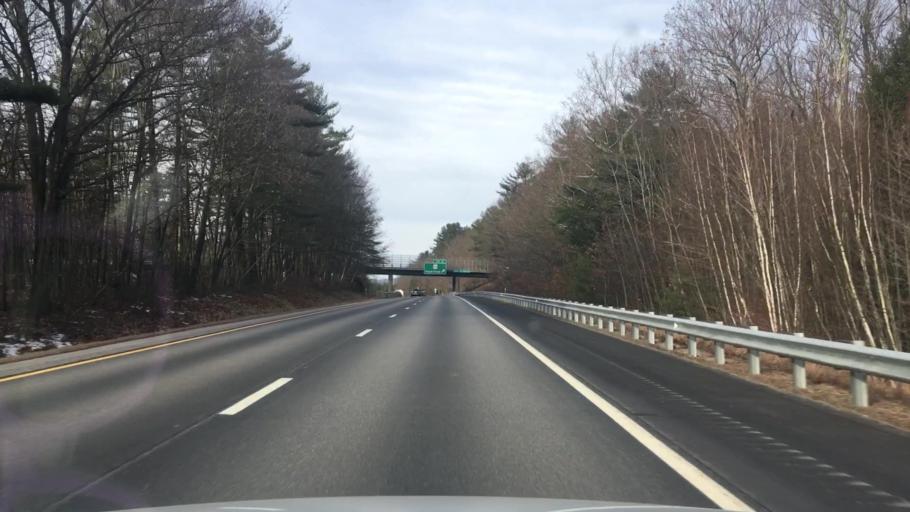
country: US
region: New Hampshire
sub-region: Merrimack County
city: Hopkinton
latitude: 43.1831
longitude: -71.6473
